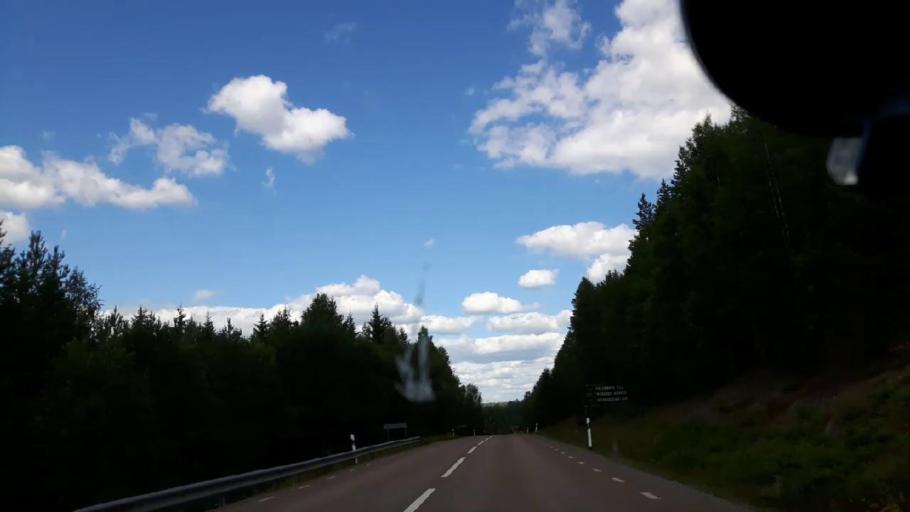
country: SE
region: Jaemtland
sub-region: Ragunda Kommun
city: Hammarstrand
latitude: 62.9914
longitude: 16.6771
